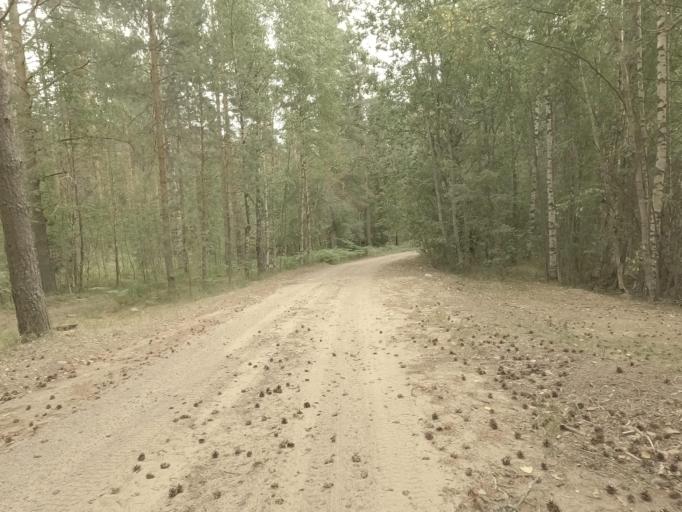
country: RU
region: Leningrad
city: Kamennogorsk
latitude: 60.9990
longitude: 29.1830
